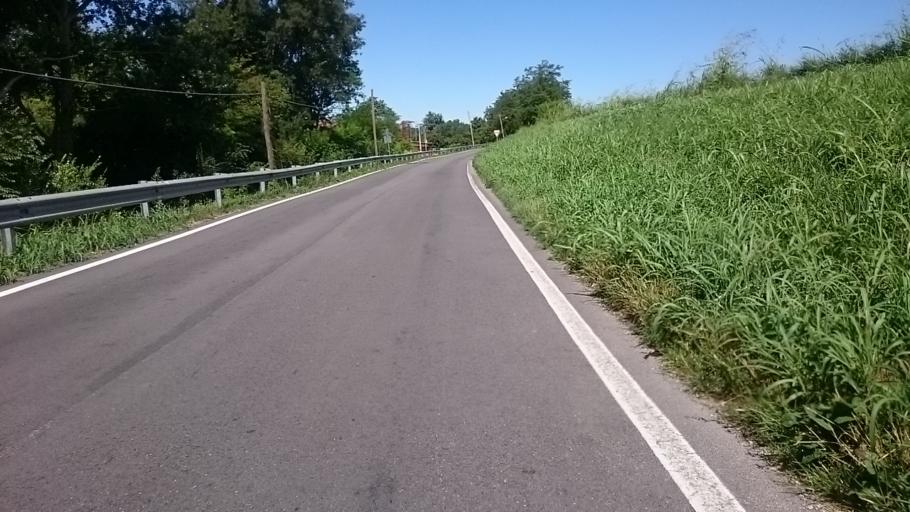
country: IT
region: Veneto
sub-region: Provincia di Padova
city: San Vito
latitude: 45.4253
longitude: 11.9534
